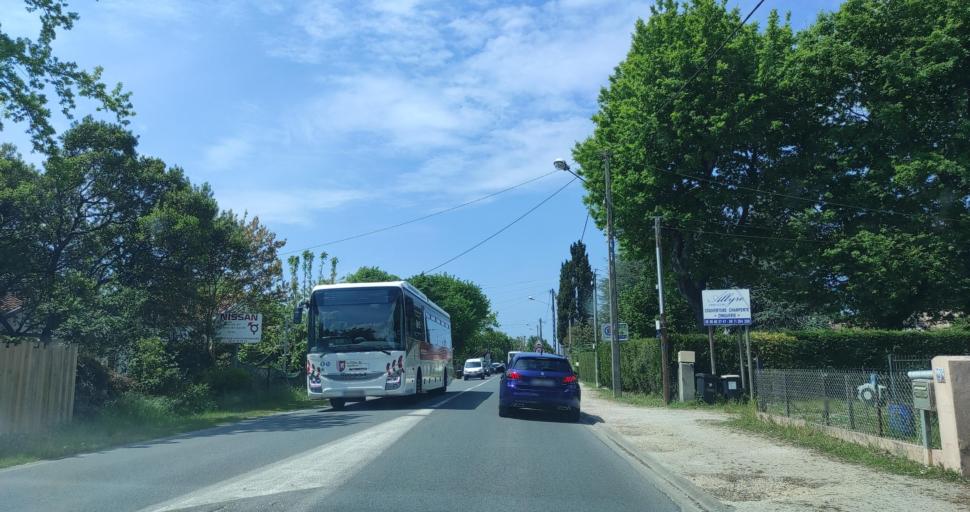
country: FR
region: Aquitaine
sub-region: Departement de la Gironde
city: Ares
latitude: 44.7621
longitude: -1.1302
